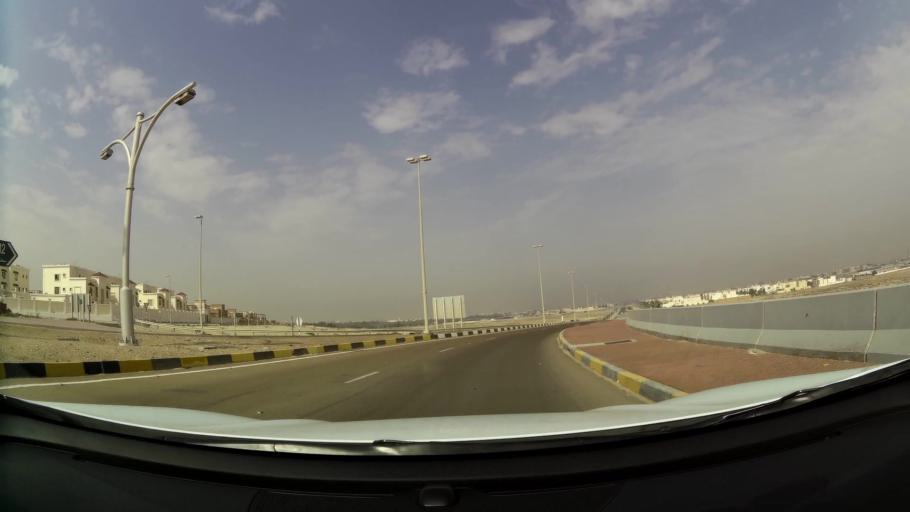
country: AE
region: Abu Dhabi
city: Abu Dhabi
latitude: 24.2769
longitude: 54.6661
